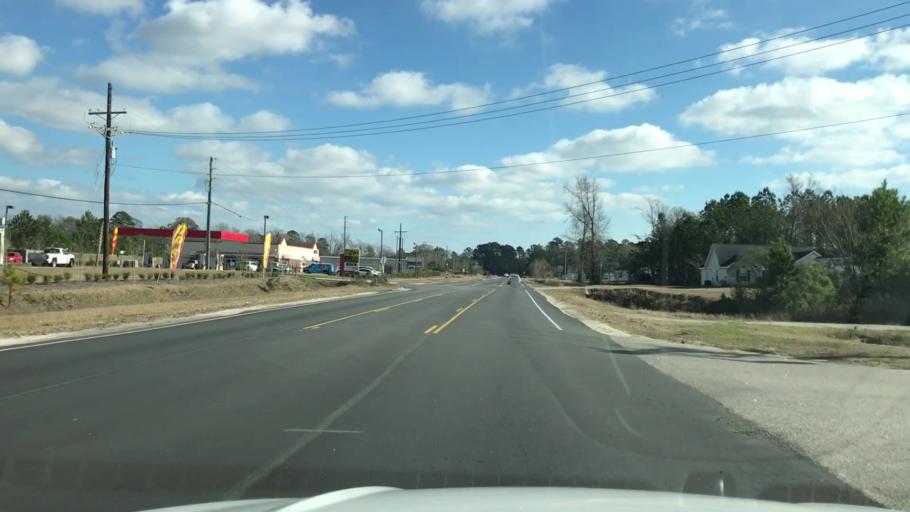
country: US
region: South Carolina
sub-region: Horry County
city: Socastee
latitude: 33.6771
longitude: -78.9768
